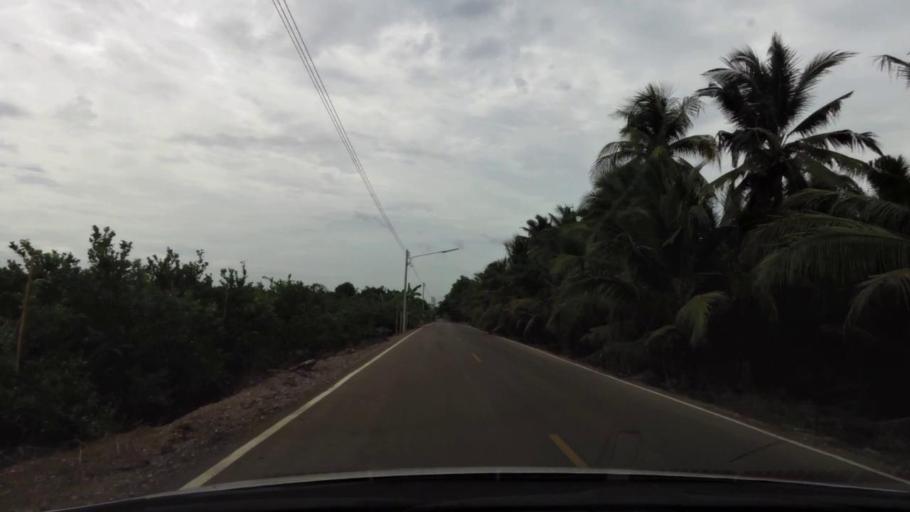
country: TH
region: Ratchaburi
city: Damnoen Saduak
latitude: 13.5497
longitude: 99.9791
